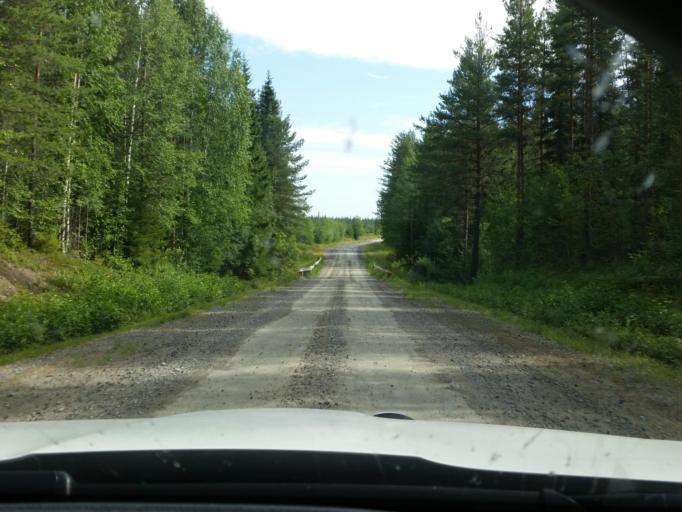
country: SE
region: Norrbotten
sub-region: Alvsbyns Kommun
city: AElvsbyn
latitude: 65.7724
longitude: 20.6926
